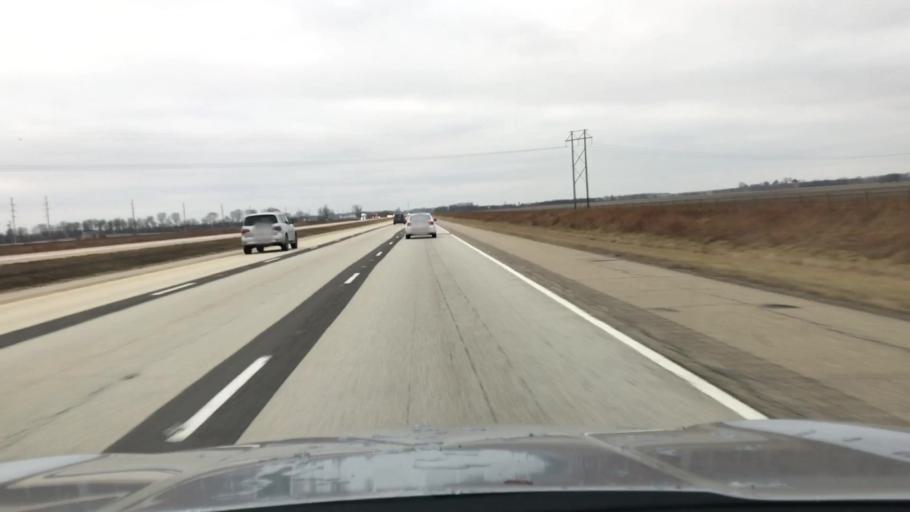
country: US
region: Illinois
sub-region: Sangamon County
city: Williamsville
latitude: 39.9926
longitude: -89.5129
